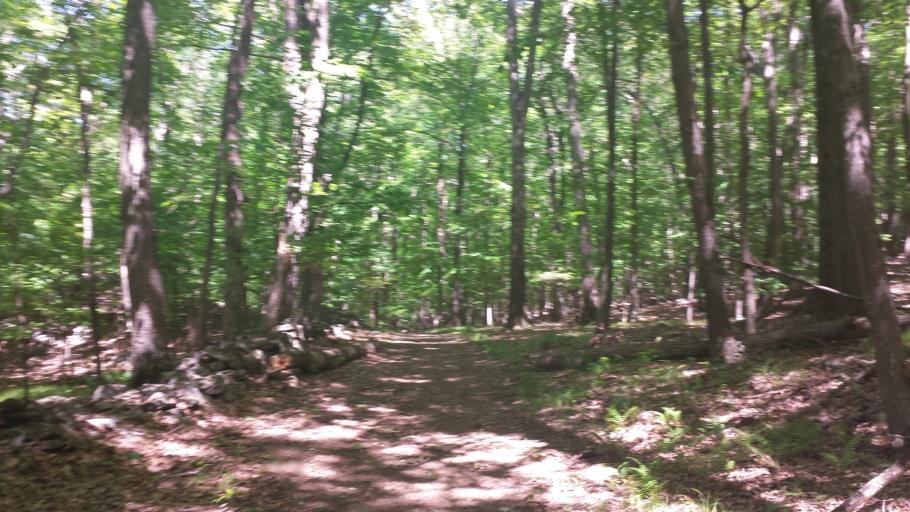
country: US
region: New York
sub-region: Westchester County
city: Pound Ridge
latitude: 41.2365
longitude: -73.5985
